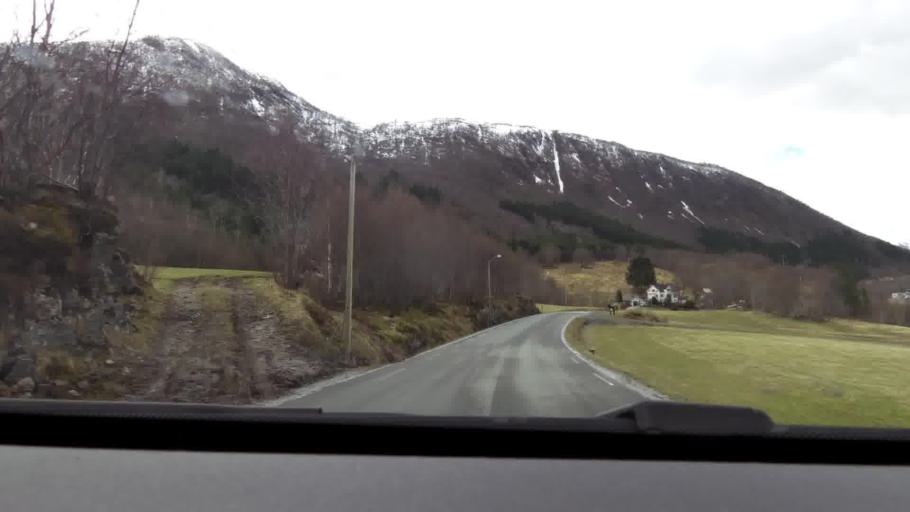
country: NO
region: More og Romsdal
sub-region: Kristiansund
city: Rensvik
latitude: 63.1106
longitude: 7.8040
